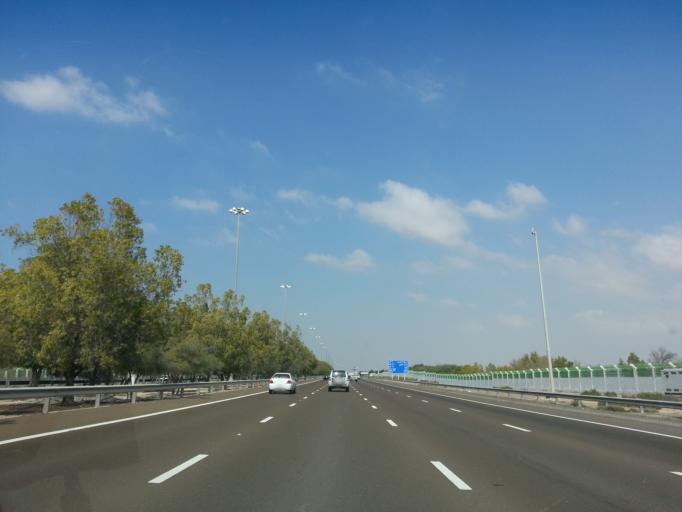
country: AE
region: Dubai
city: Dubai
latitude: 24.8392
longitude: 54.8891
